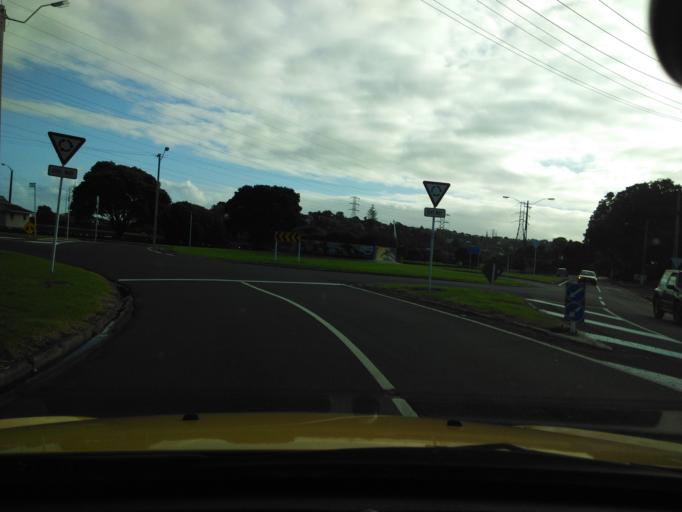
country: NZ
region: Auckland
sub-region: Auckland
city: Mangere
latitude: -36.9236
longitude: 174.7773
